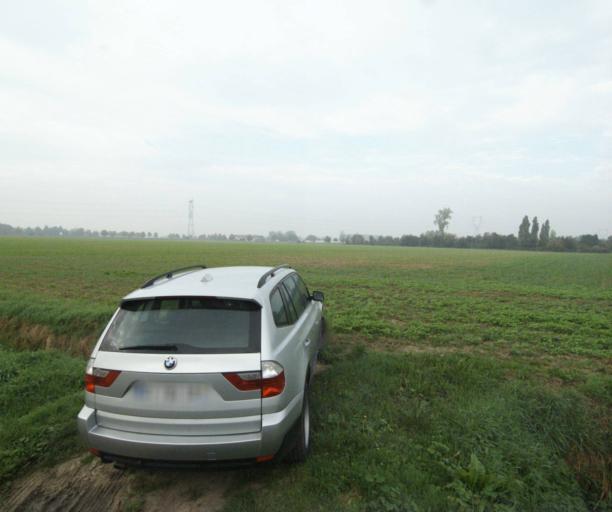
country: FR
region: Nord-Pas-de-Calais
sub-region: Departement du Nord
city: Seclin
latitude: 50.5379
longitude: 3.0223
